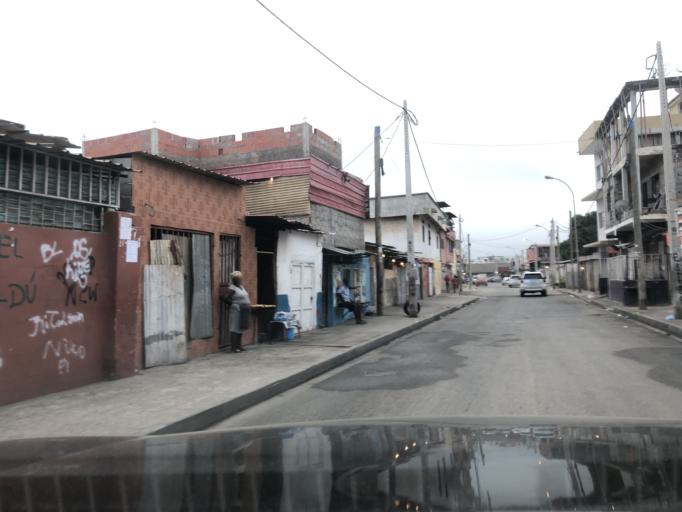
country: AO
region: Luanda
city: Luanda
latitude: -8.8428
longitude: 13.2304
